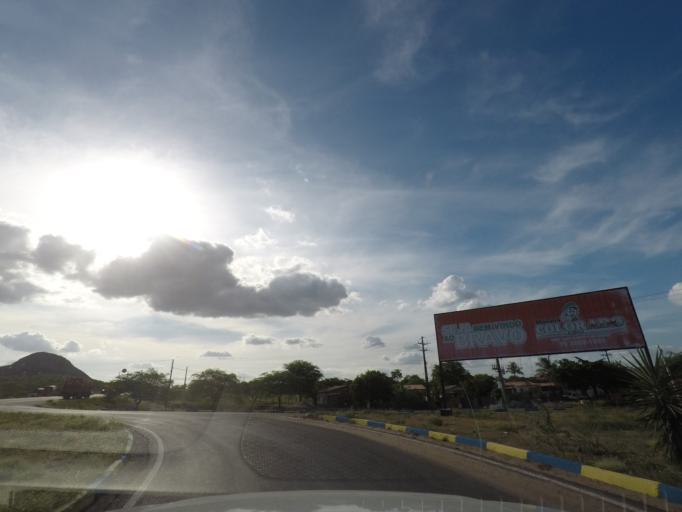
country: BR
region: Bahia
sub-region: Anguera
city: Anguera
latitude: -12.1806
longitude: -39.4532
